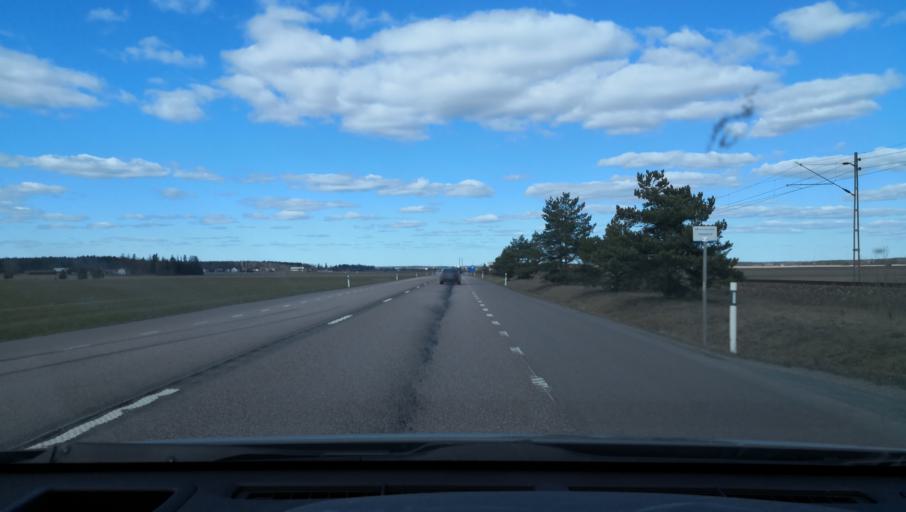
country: SE
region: Vaestmanland
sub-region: Sala Kommun
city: Sala
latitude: 59.8789
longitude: 16.6257
